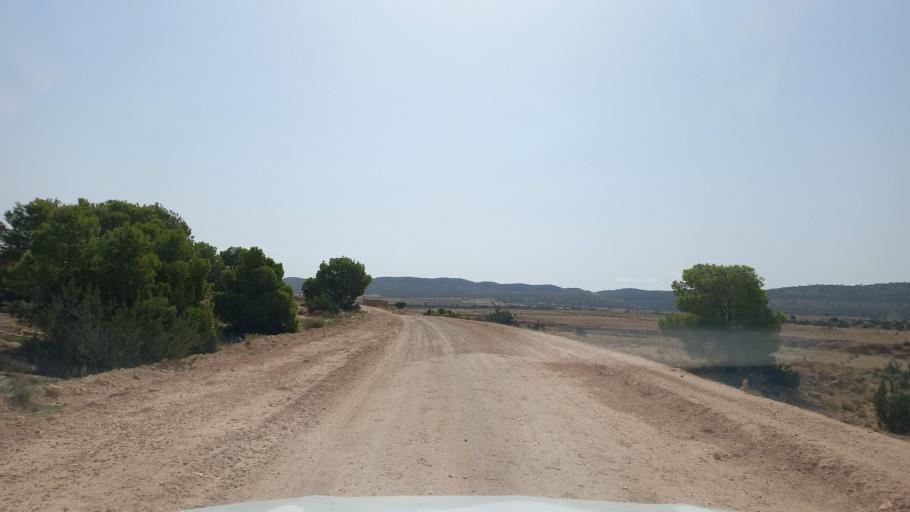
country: TN
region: Al Qasrayn
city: Sbiba
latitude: 35.3949
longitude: 8.9513
